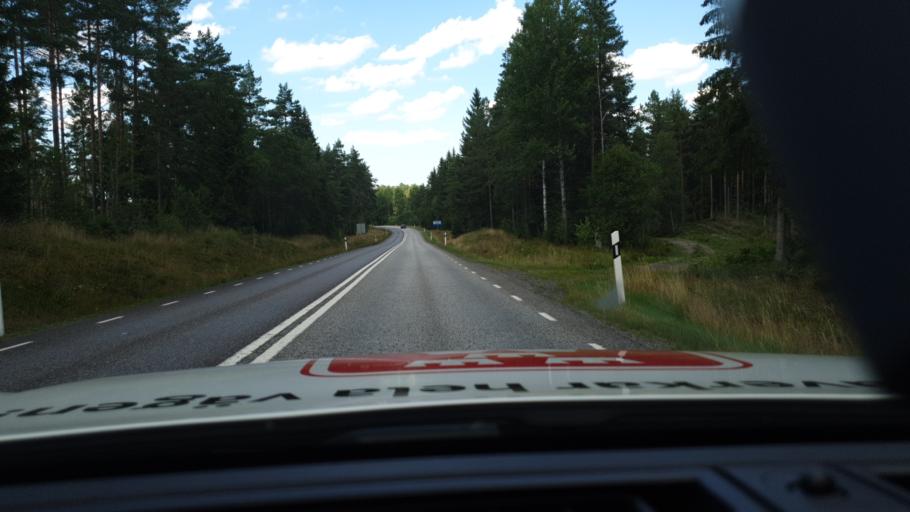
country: SE
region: Joenkoeping
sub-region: Vaggeryds Kommun
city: Vaggeryd
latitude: 57.5287
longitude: 14.2745
